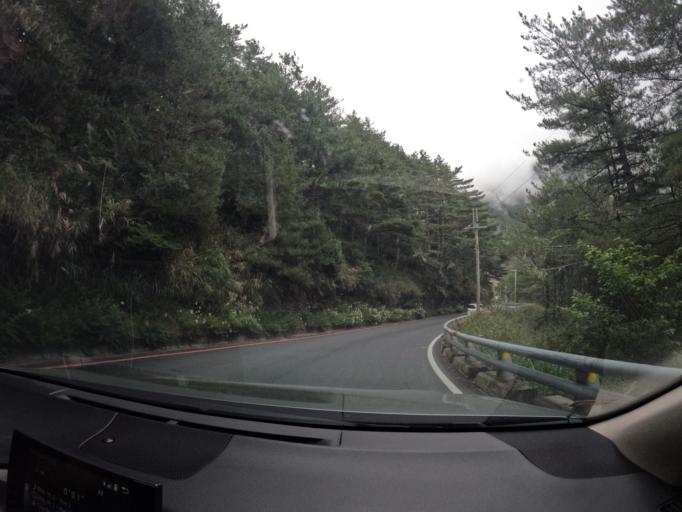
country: TW
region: Taiwan
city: Lugu
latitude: 23.2692
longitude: 120.9723
